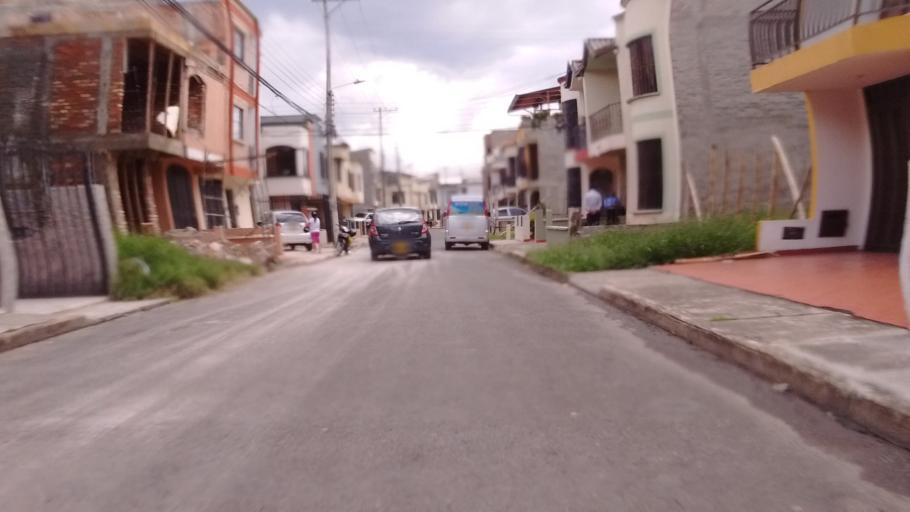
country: CO
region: Cauca
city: Popayan
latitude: 2.4601
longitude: -76.5910
